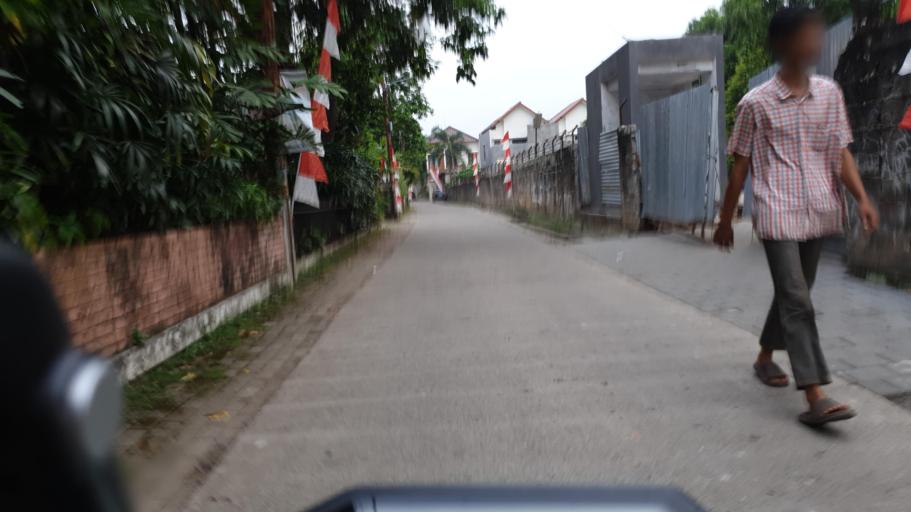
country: ID
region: West Java
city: Pamulang
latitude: -6.3187
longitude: 106.7706
